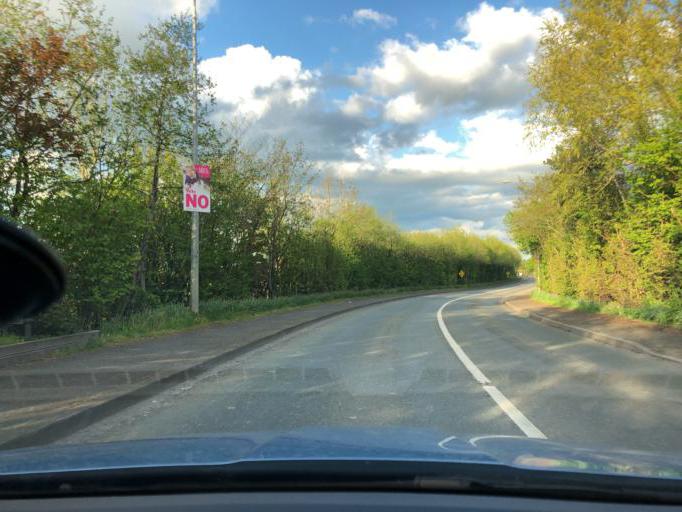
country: IE
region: Leinster
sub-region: Kildare
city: Kilcock
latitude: 53.3971
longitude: -6.6801
